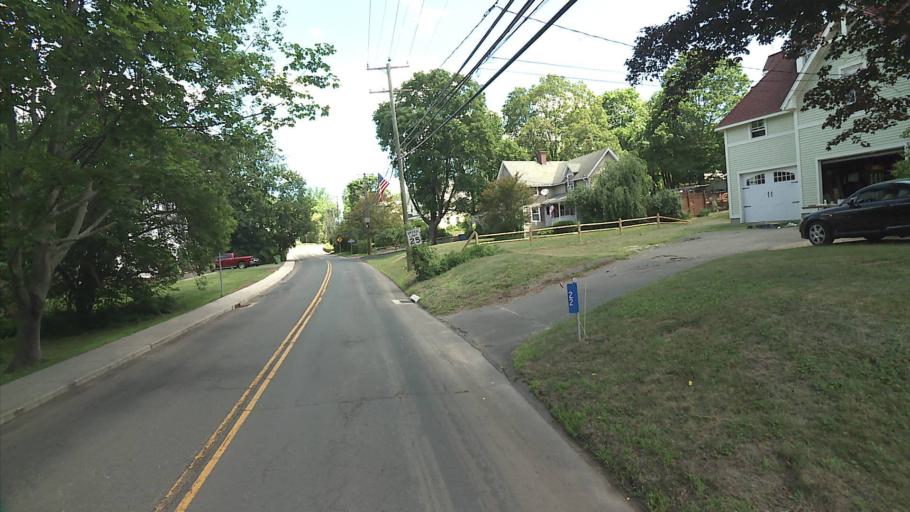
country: US
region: Connecticut
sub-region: Middlesex County
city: East Hampton
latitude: 41.5782
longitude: -72.4983
